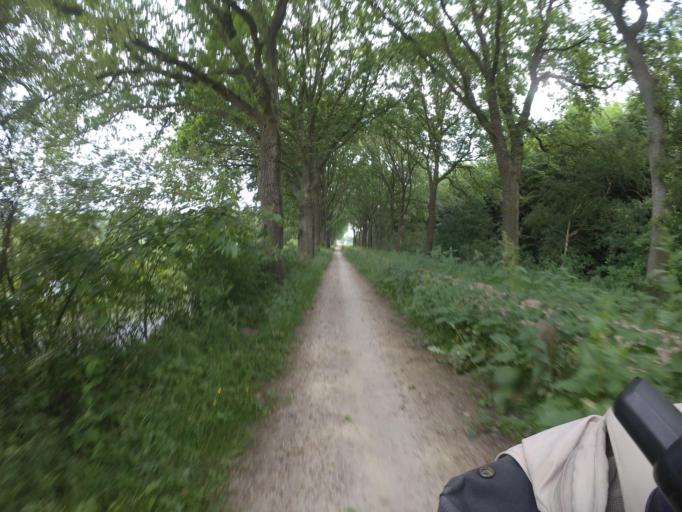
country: NL
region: Drenthe
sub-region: Gemeente Assen
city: Assen
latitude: 53.0115
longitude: 6.4378
